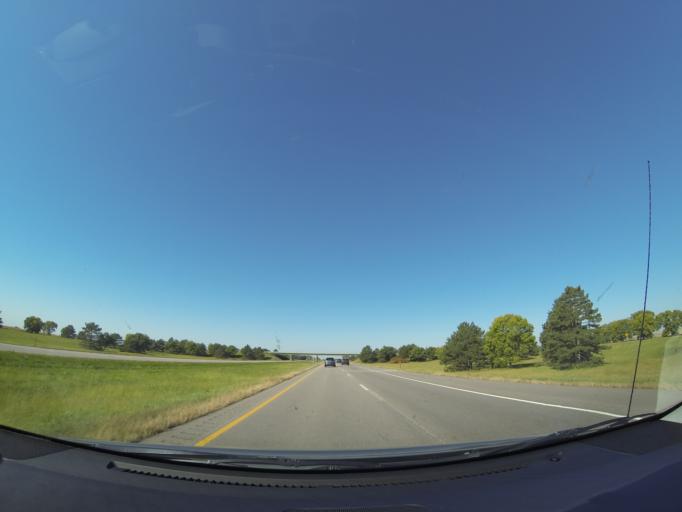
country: US
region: Nebraska
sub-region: Saline County
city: Friend
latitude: 40.8221
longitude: -97.2885
